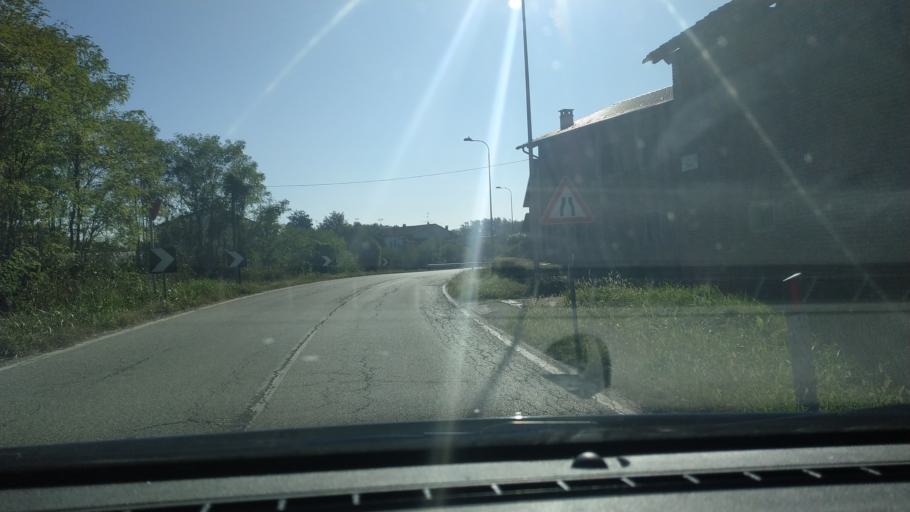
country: IT
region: Piedmont
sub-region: Provincia di Torino
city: Verolengo
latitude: 45.1947
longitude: 7.9477
